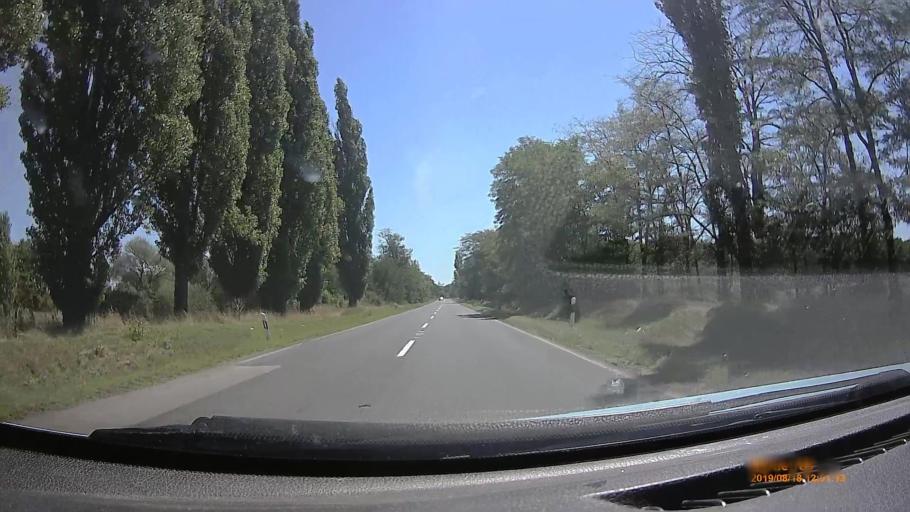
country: HU
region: Fejer
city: Aba
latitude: 47.0760
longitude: 18.5066
